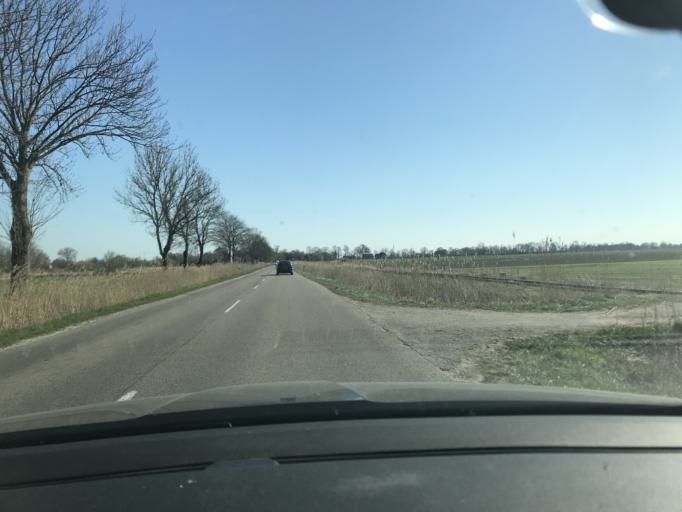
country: PL
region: Pomeranian Voivodeship
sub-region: Powiat nowodworski
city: Nowy Dwor Gdanski
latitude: 54.2489
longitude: 19.1404
